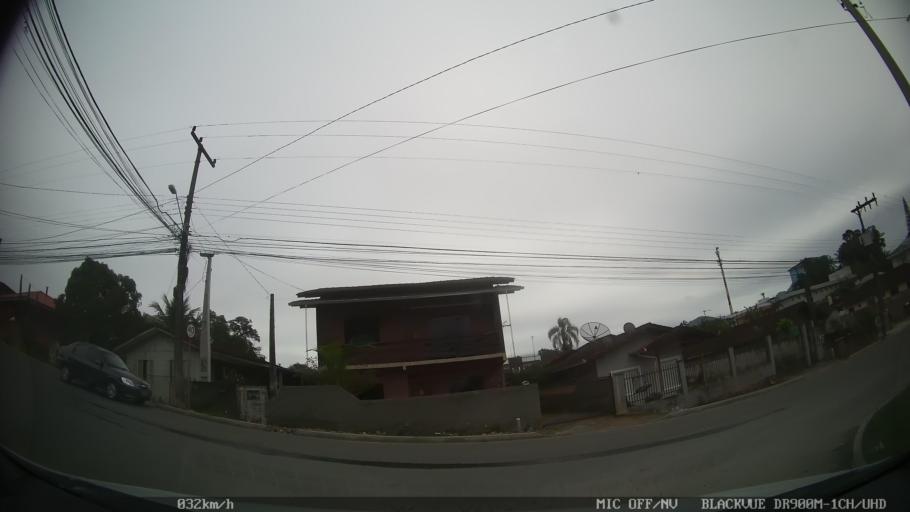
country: BR
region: Santa Catarina
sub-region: Joinville
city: Joinville
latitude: -26.2916
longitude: -48.9032
